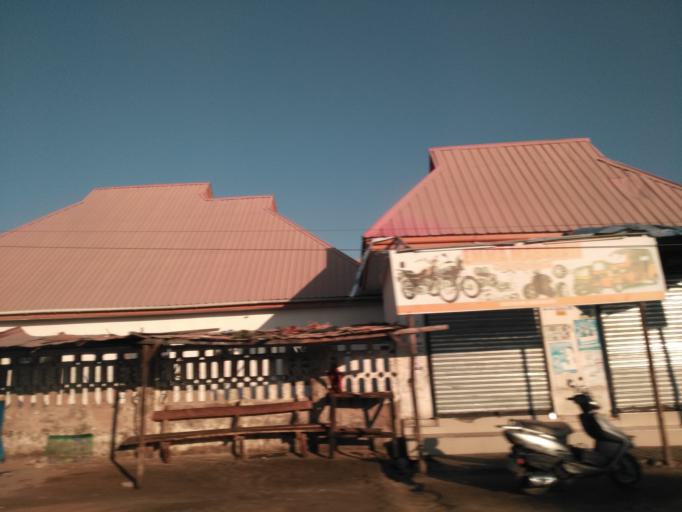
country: TZ
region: Dodoma
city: Dodoma
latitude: -6.1723
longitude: 35.7360
